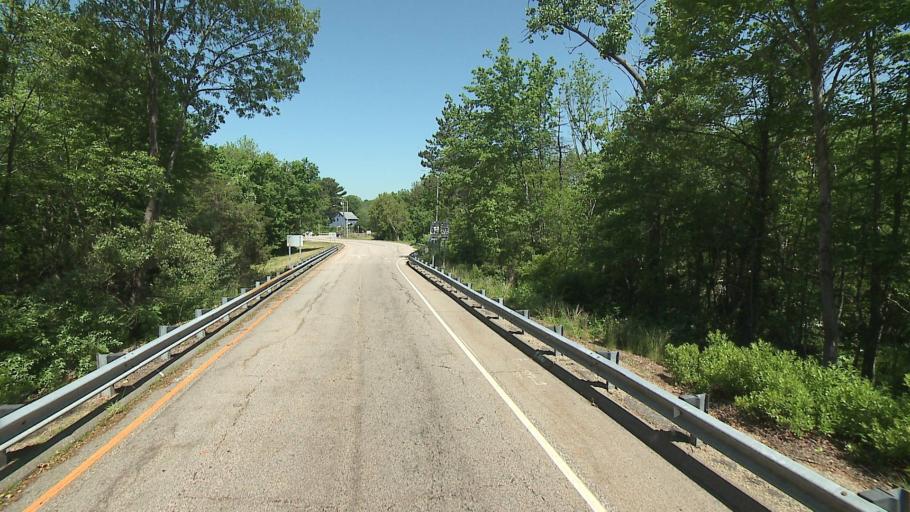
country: US
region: Connecticut
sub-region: New London County
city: Norwich
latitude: 41.4828
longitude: -72.0978
